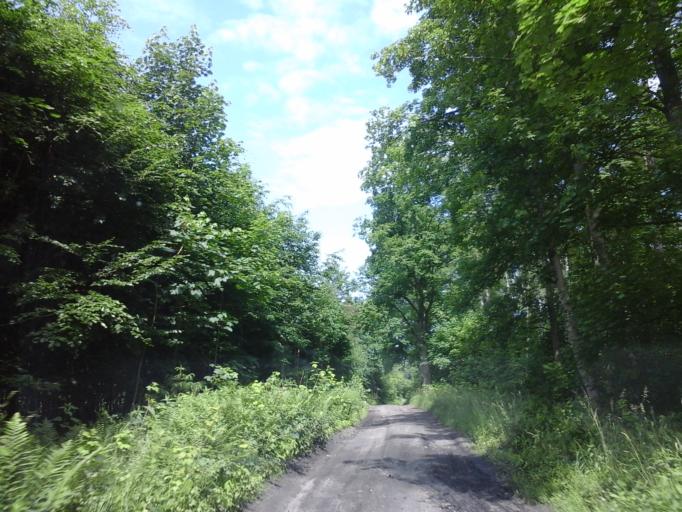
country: PL
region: West Pomeranian Voivodeship
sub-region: Powiat stargardzki
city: Dolice
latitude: 53.2114
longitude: 15.2607
